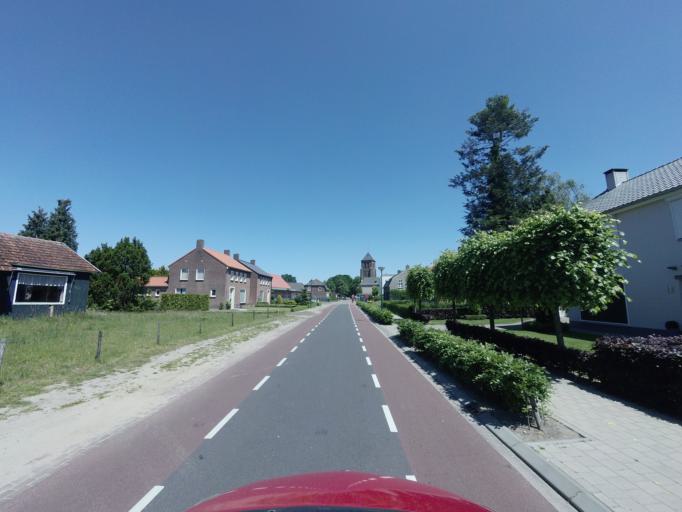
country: NL
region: North Brabant
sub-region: Bergeijk
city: Bergeyk
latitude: 51.2886
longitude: 5.3184
